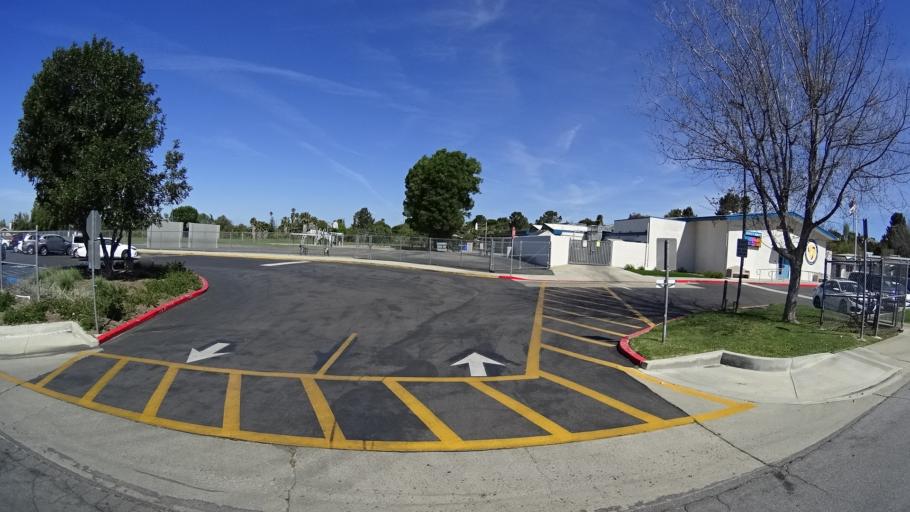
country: US
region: California
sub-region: Ventura County
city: Thousand Oaks
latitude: 34.2169
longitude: -118.8581
